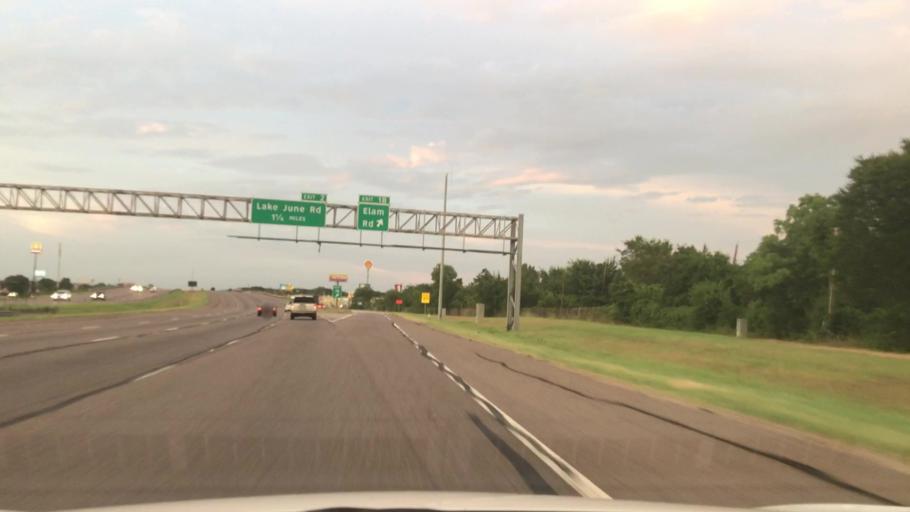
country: US
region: Texas
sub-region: Dallas County
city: Balch Springs
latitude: 32.7156
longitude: -96.6176
